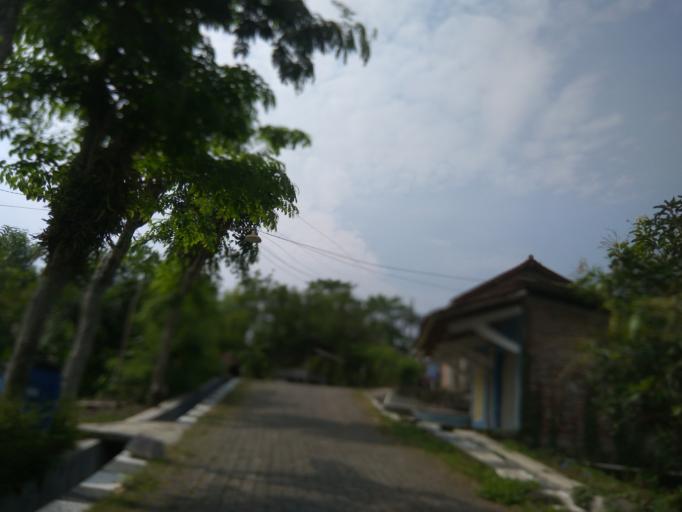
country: ID
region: Central Java
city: Semarang
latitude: -7.0345
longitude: 110.4066
